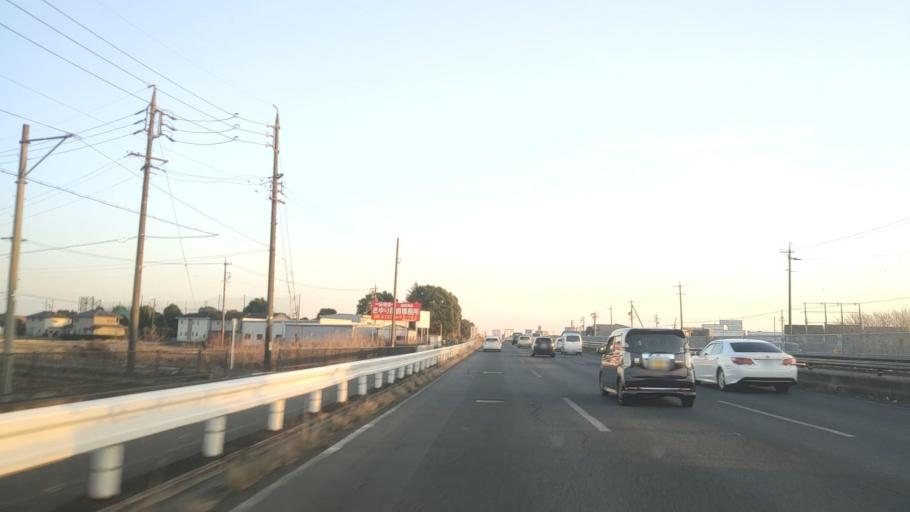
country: JP
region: Aichi
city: Kuroda
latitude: 35.3329
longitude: 136.8025
